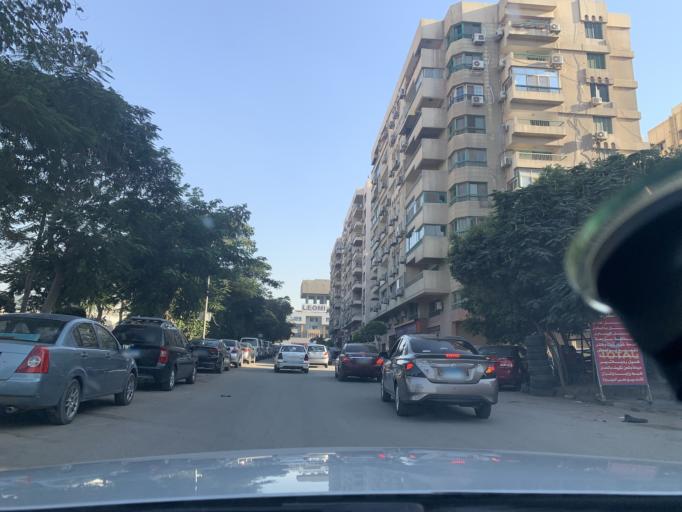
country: EG
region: Muhafazat al Qahirah
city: Cairo
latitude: 30.0370
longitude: 31.3465
